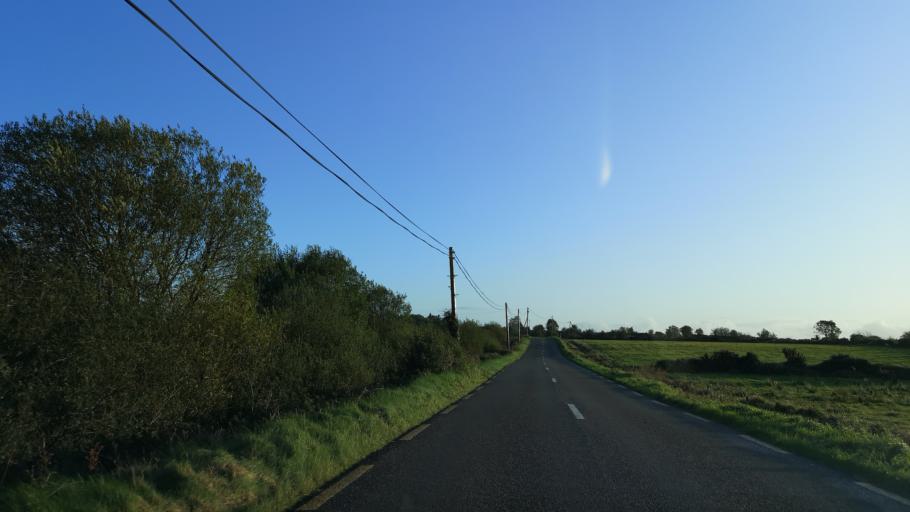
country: IE
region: Connaught
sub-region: Roscommon
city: Castlerea
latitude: 53.7055
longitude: -8.5655
